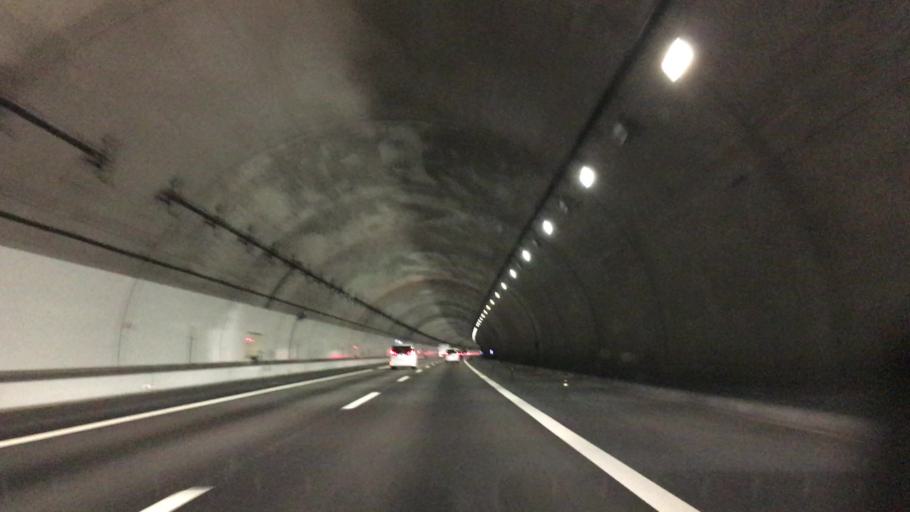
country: JP
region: Shiga Prefecture
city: Minakuchicho-matoba
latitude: 34.9231
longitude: 136.1169
